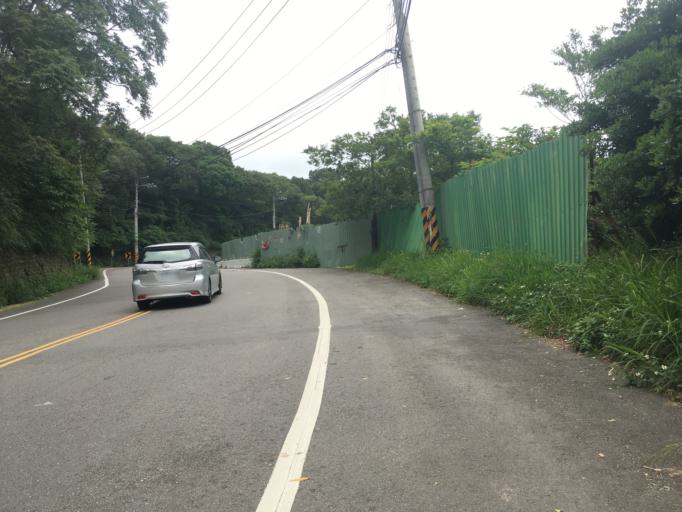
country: TW
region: Taiwan
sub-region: Hsinchu
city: Hsinchu
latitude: 24.7491
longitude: 120.9767
